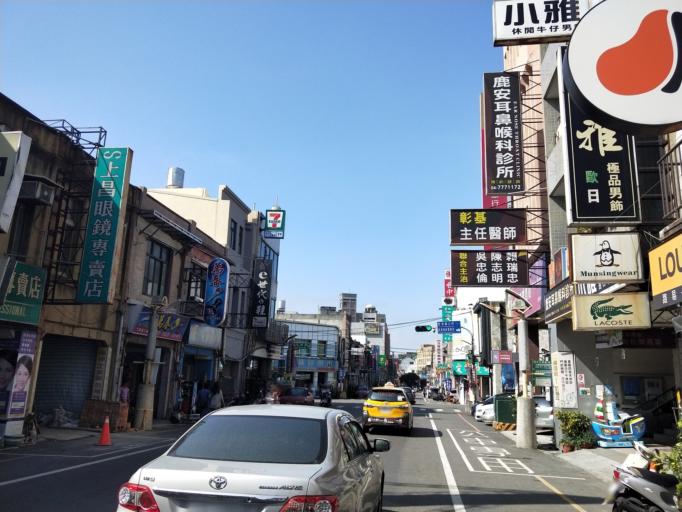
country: TW
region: Taiwan
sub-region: Changhua
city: Chang-hua
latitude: 24.0556
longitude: 120.4342
